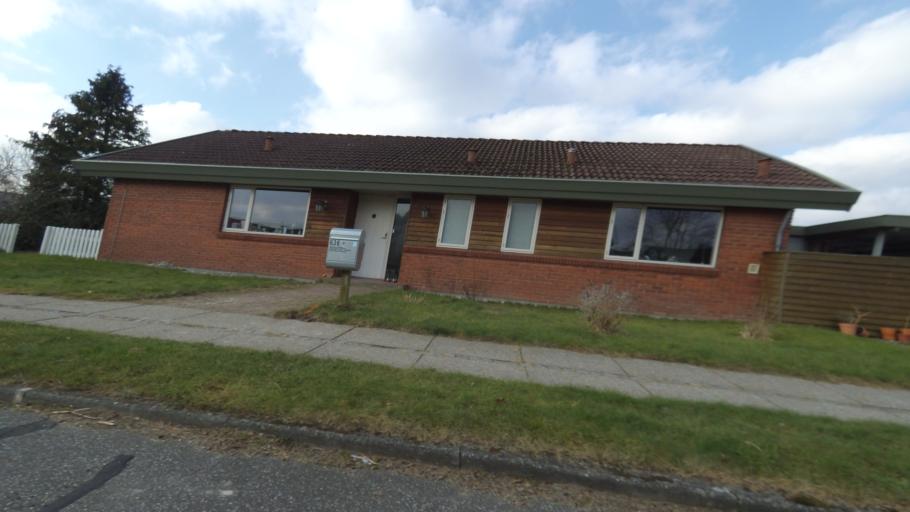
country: DK
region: Central Jutland
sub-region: Arhus Kommune
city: Tranbjerg
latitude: 56.0916
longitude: 10.1206
